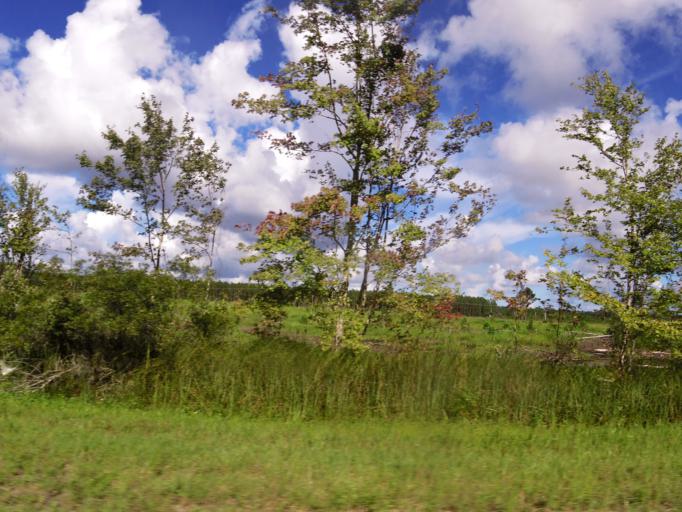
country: US
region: Georgia
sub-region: Camden County
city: Kingsland
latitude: 30.8817
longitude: -81.7065
